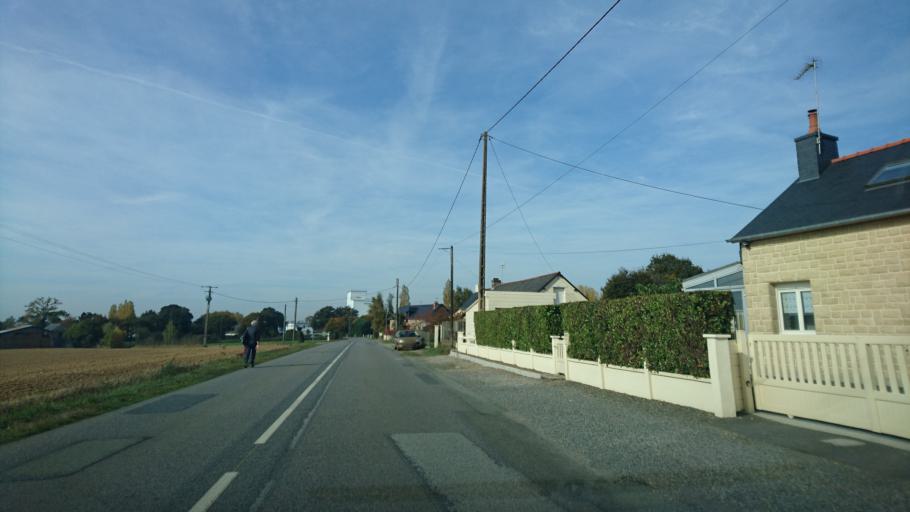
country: FR
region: Brittany
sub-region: Departement d'Ille-et-Vilaine
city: Janze
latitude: 47.9679
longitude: -1.5273
